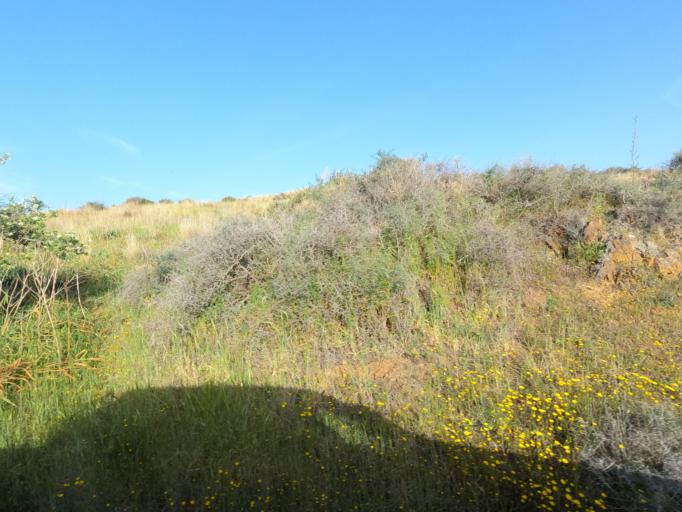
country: CY
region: Lefkosia
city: Lefka
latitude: 35.0825
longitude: 32.9355
